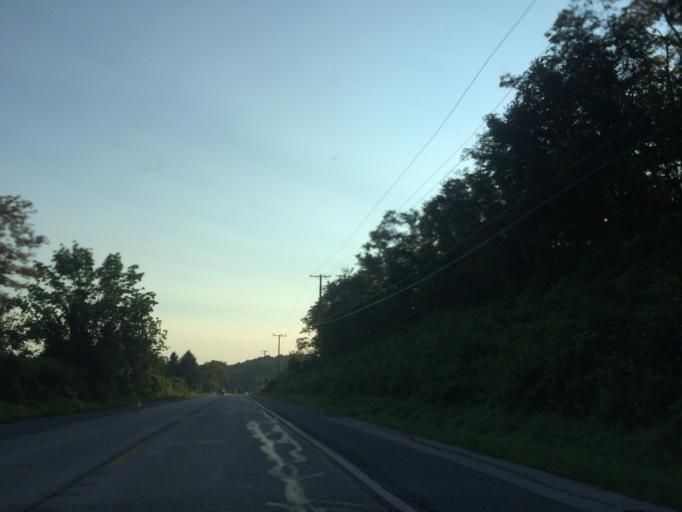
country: US
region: Maryland
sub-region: Carroll County
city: Manchester
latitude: 39.6472
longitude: -76.9136
